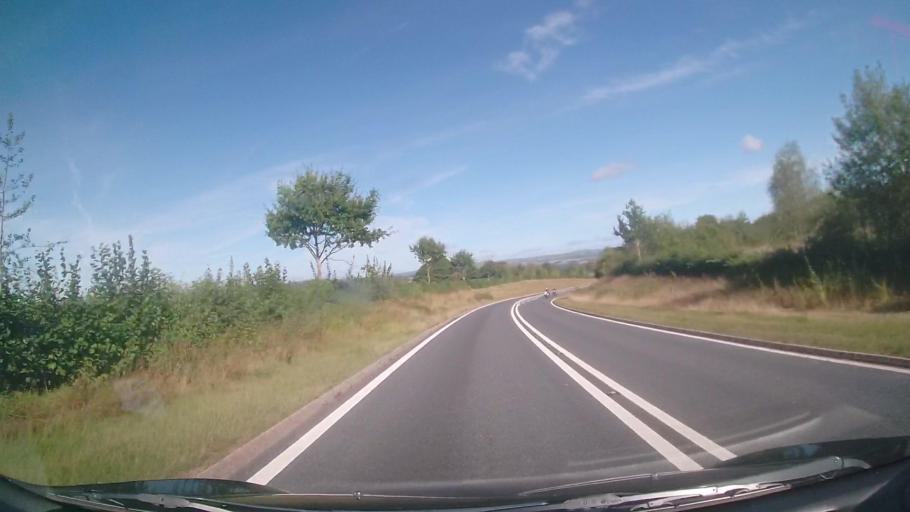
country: GB
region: Wales
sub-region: Sir Powys
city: Hay
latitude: 51.9846
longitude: -3.2340
